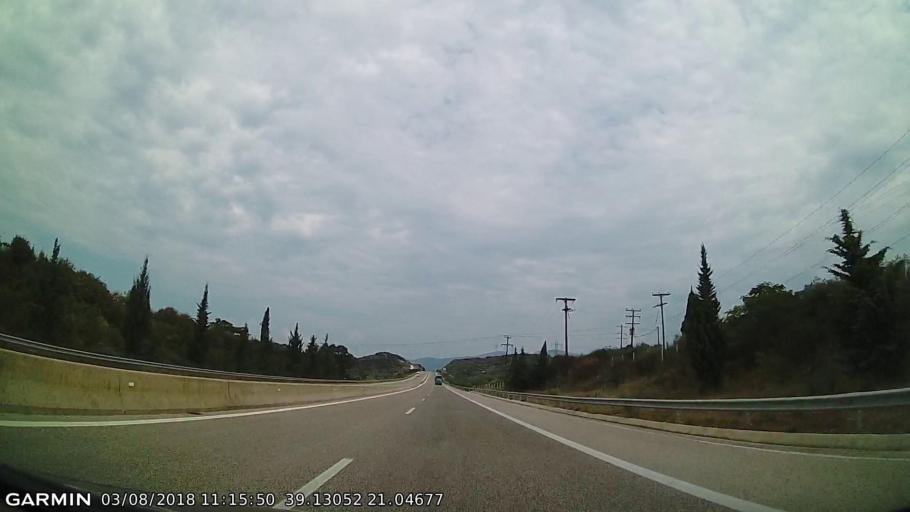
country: GR
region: Epirus
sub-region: Nomos Artas
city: Peta
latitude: 39.1305
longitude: 21.0468
